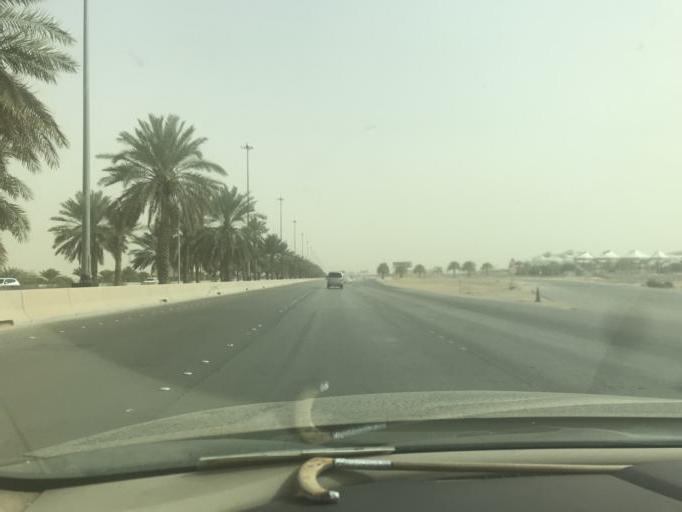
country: SA
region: Ar Riyad
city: Riyadh
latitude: 24.8823
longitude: 46.7216
